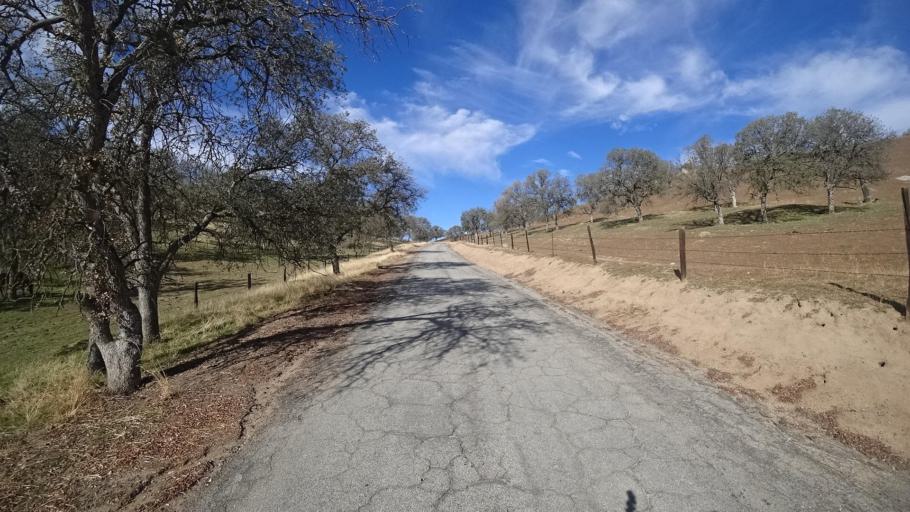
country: US
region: California
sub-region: Kern County
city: Oildale
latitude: 35.5651
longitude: -118.7963
